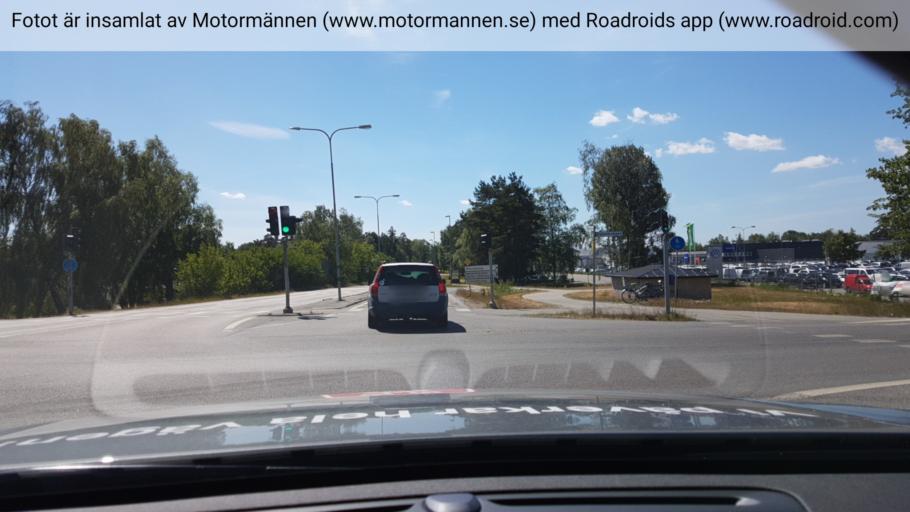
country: SE
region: Stockholm
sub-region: Haninge Kommun
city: Haninge
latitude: 59.1671
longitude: 18.1627
